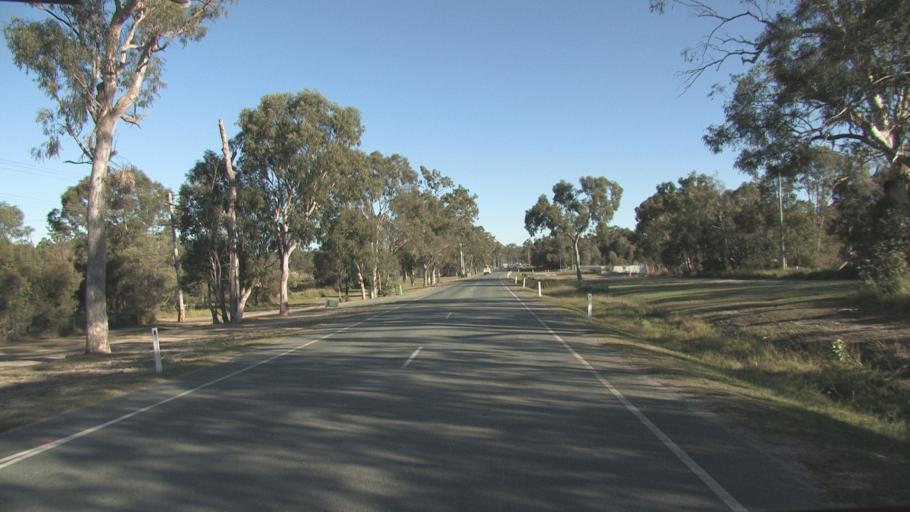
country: AU
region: Queensland
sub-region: Logan
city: Logan Reserve
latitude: -27.7136
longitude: 153.0929
